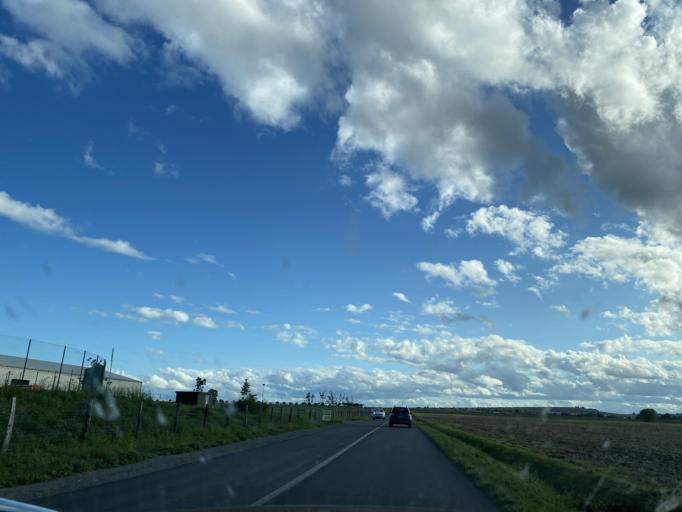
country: FR
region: Auvergne
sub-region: Departement de l'Allier
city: Gannat
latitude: 46.1031
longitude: 3.2606
